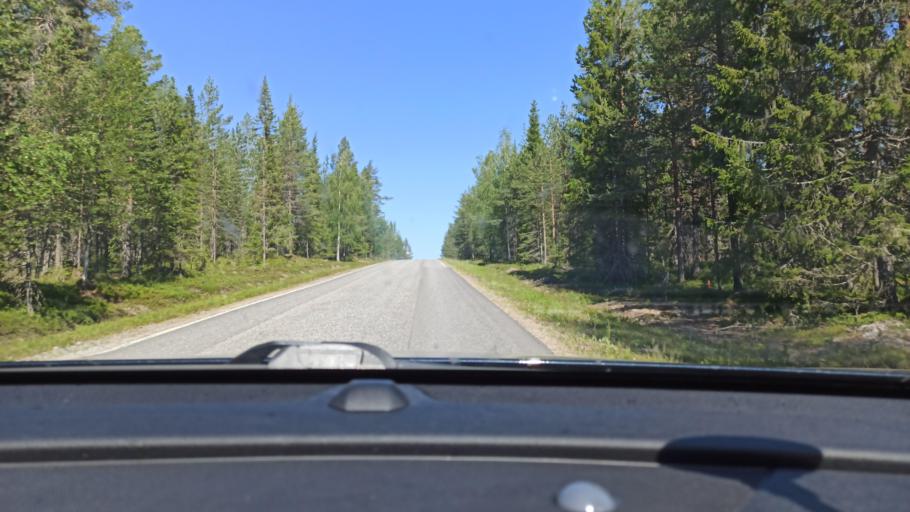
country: FI
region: Lapland
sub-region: Tunturi-Lappi
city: Kolari
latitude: 67.6789
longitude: 24.1403
